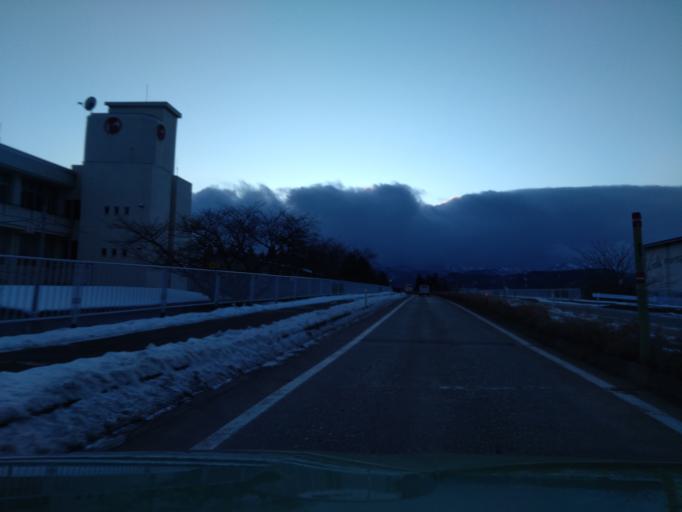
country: JP
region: Iwate
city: Shizukuishi
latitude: 39.7025
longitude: 140.9646
